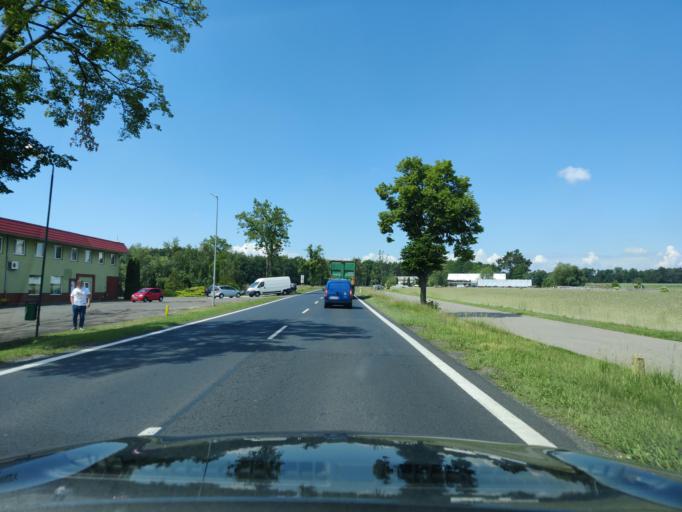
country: PL
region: Greater Poland Voivodeship
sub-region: Powiat grodziski
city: Rakoniewice
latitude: 52.1338
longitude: 16.2520
